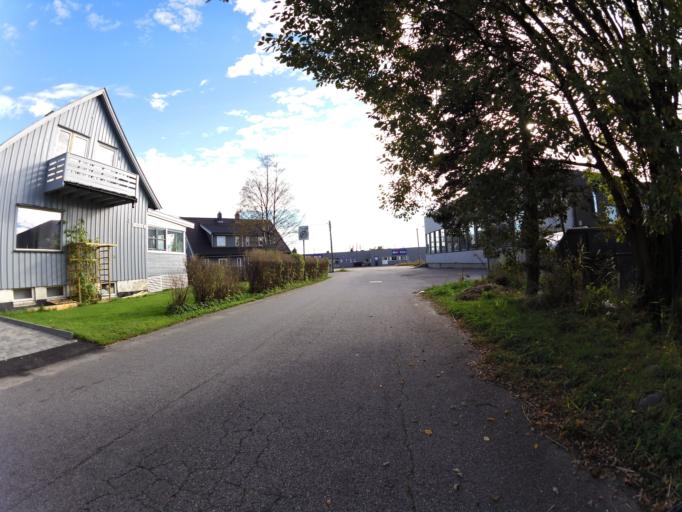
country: NO
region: Ostfold
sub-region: Sarpsborg
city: Sarpsborg
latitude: 59.2889
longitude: 11.0903
